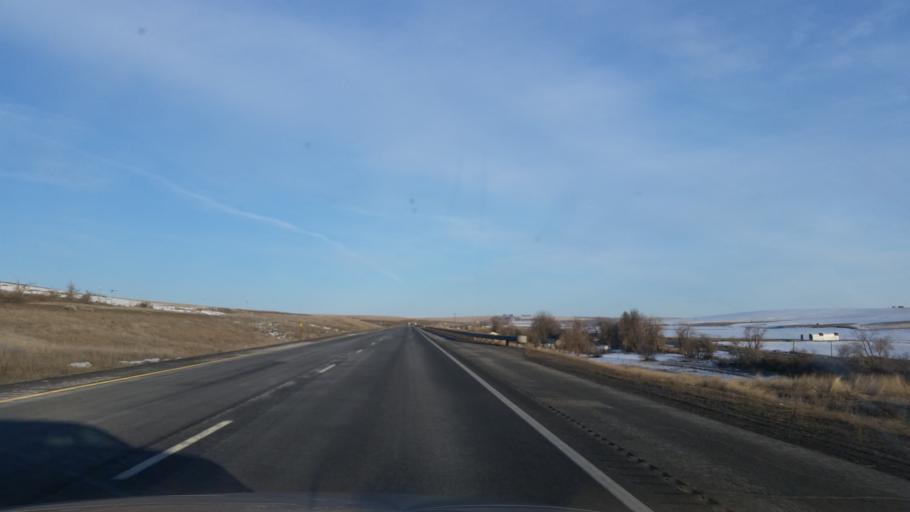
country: US
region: Washington
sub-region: Grant County
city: Warden
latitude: 47.0849
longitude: -118.9472
